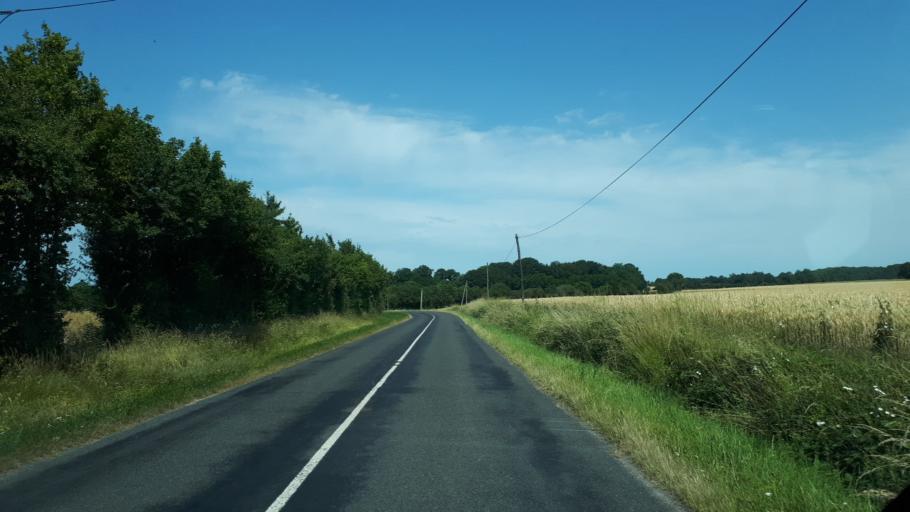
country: FR
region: Centre
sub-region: Departement du Loir-et-Cher
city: La Ville-aux-Clercs
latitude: 47.9596
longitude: 1.0724
